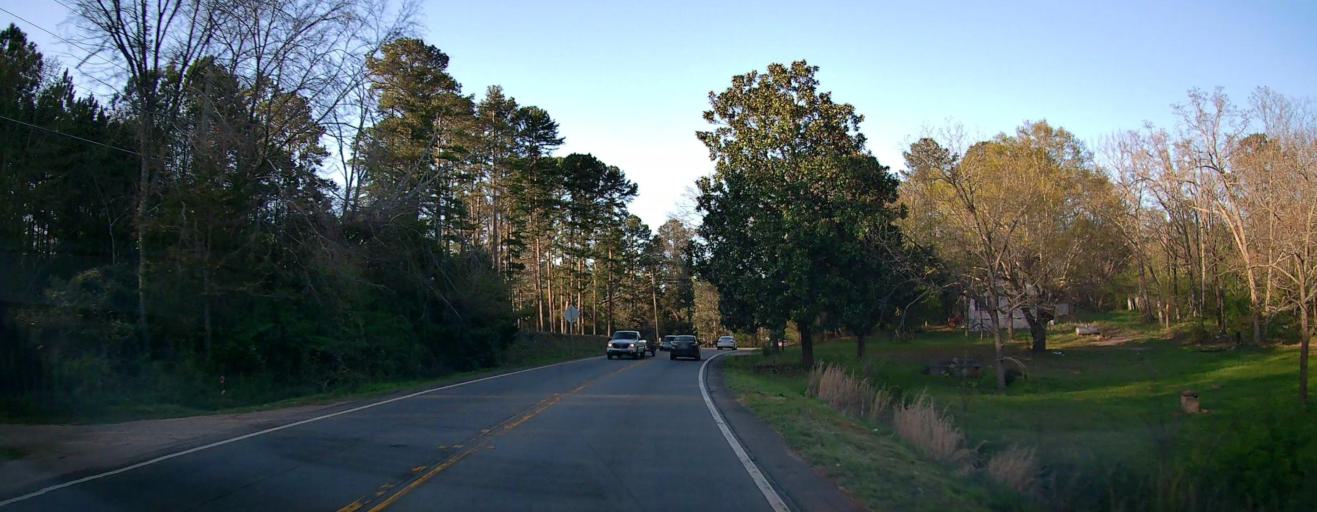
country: US
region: Georgia
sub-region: Newton County
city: Porterdale
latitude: 33.5391
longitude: -83.9176
